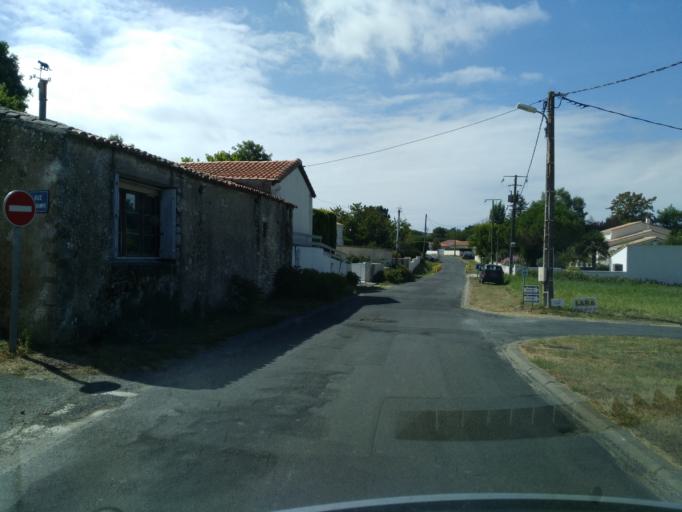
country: FR
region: Poitou-Charentes
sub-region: Departement de la Charente-Maritime
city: Saint-Palais-sur-Mer
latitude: 45.6767
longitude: -1.0871
